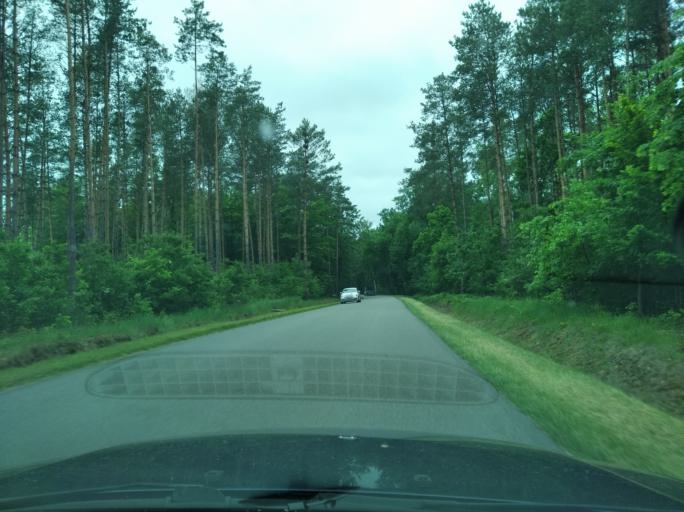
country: PL
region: Subcarpathian Voivodeship
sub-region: Powiat kolbuszowski
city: Niwiska
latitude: 50.2018
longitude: 21.6520
